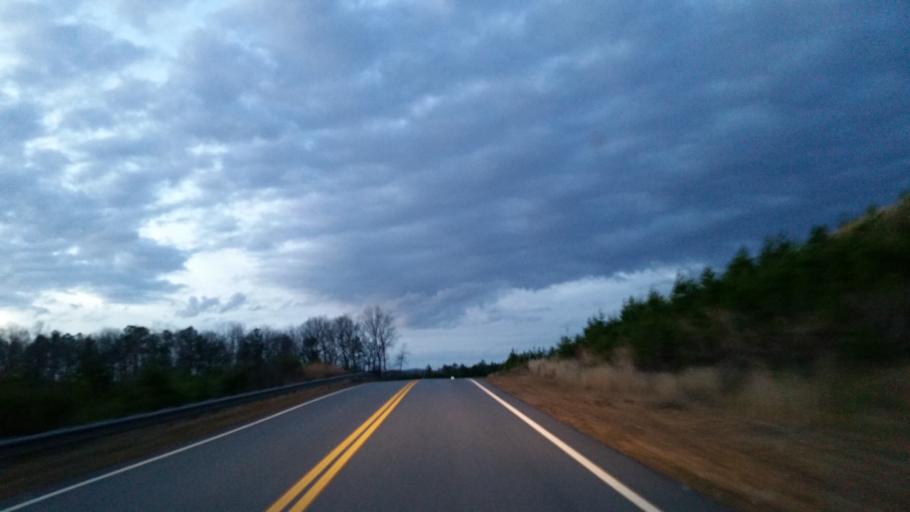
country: US
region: Georgia
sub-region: Cherokee County
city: Ball Ground
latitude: 34.3079
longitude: -84.4294
